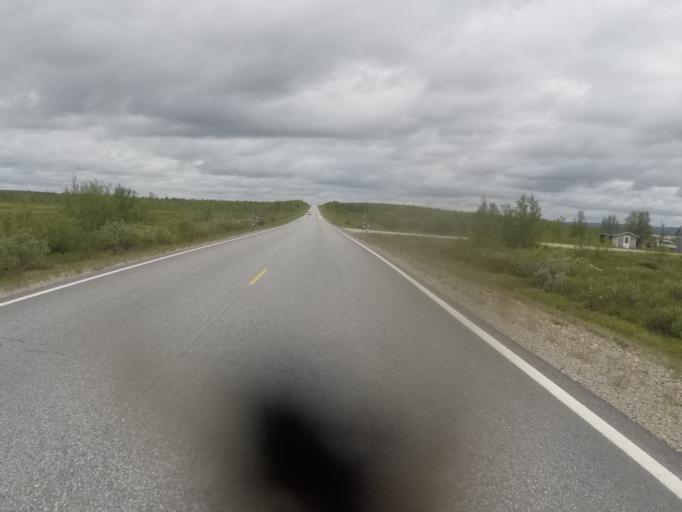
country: NO
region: Finnmark Fylke
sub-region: Kautokeino
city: Kautokeino
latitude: 68.7904
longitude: 23.2974
